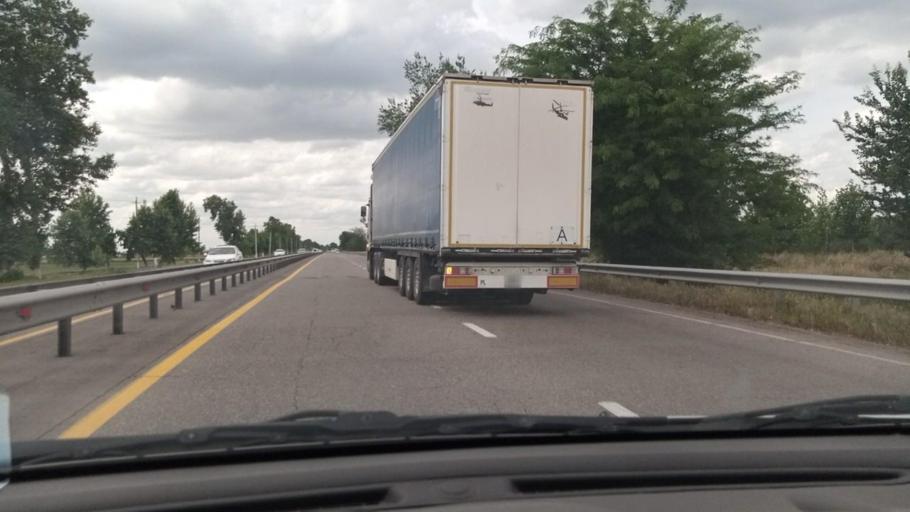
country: UZ
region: Toshkent Shahri
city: Bektemir
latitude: 41.1681
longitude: 69.4157
